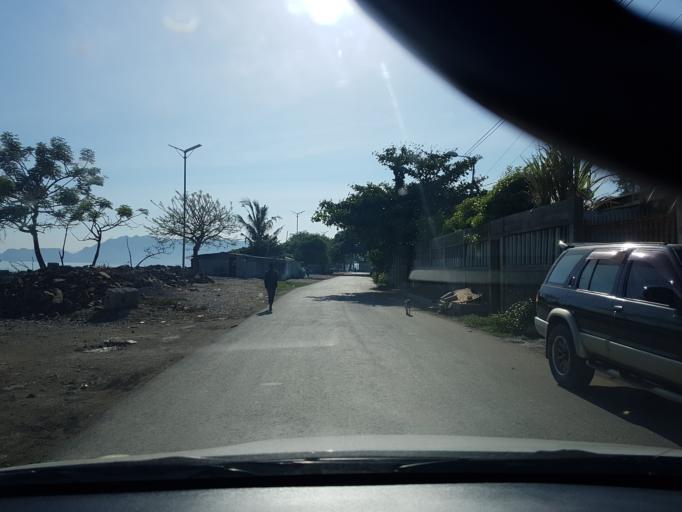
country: TL
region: Dili
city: Dili
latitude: -8.5408
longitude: 125.5415
